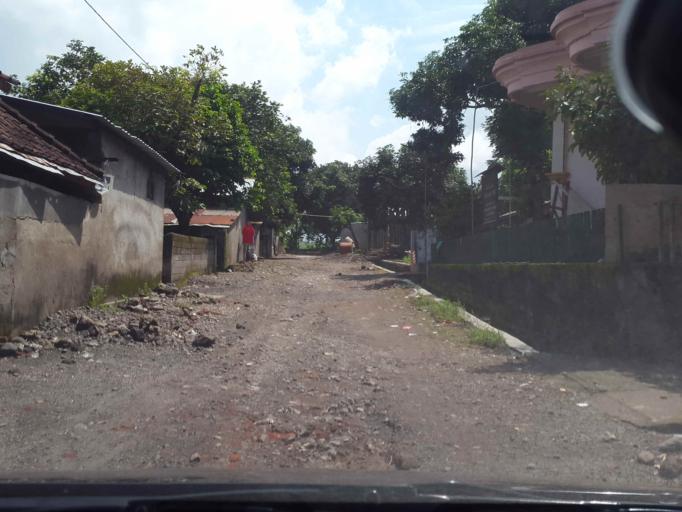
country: ID
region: West Nusa Tenggara
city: Jejelok
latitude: -8.6054
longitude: 116.1705
